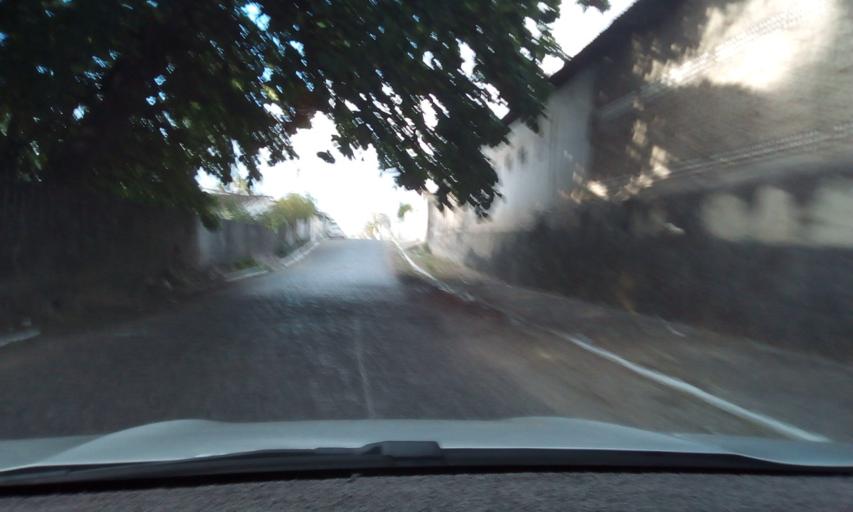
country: BR
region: Paraiba
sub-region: Joao Pessoa
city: Joao Pessoa
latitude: -7.1451
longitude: -34.8924
